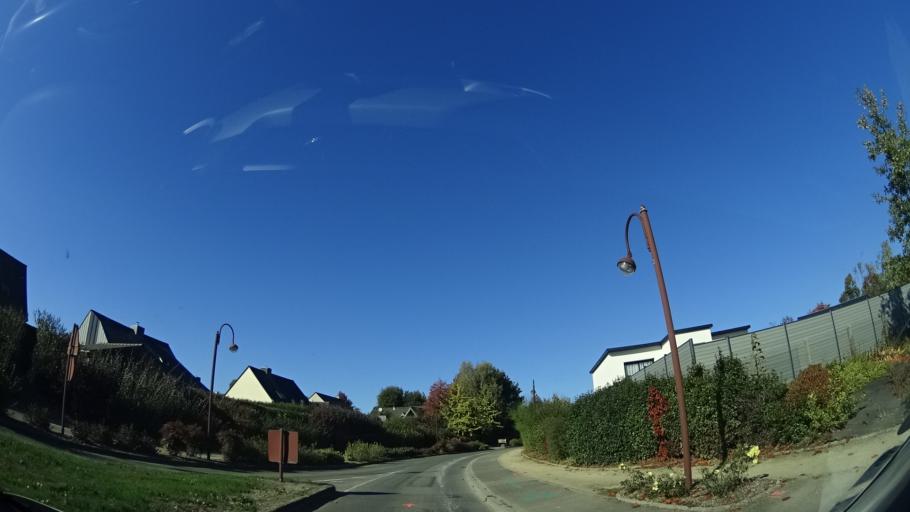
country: FR
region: Brittany
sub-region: Departement d'Ille-et-Vilaine
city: La Meziere
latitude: 48.2146
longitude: -1.7550
